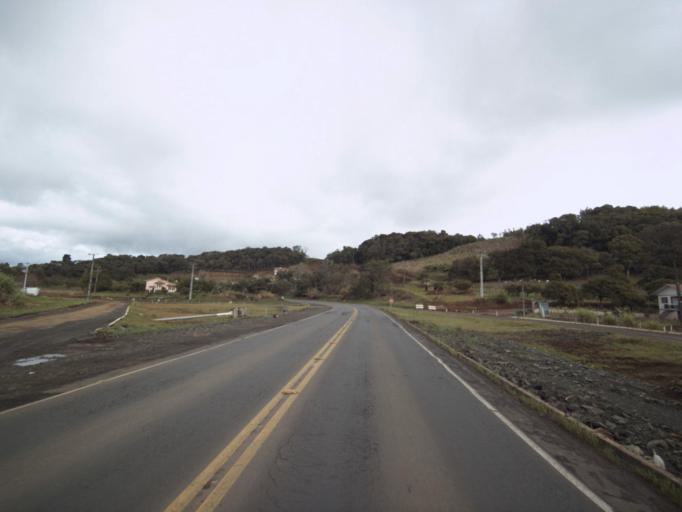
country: BR
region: Santa Catarina
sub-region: Concordia
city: Concordia
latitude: -27.2285
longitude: -51.9524
